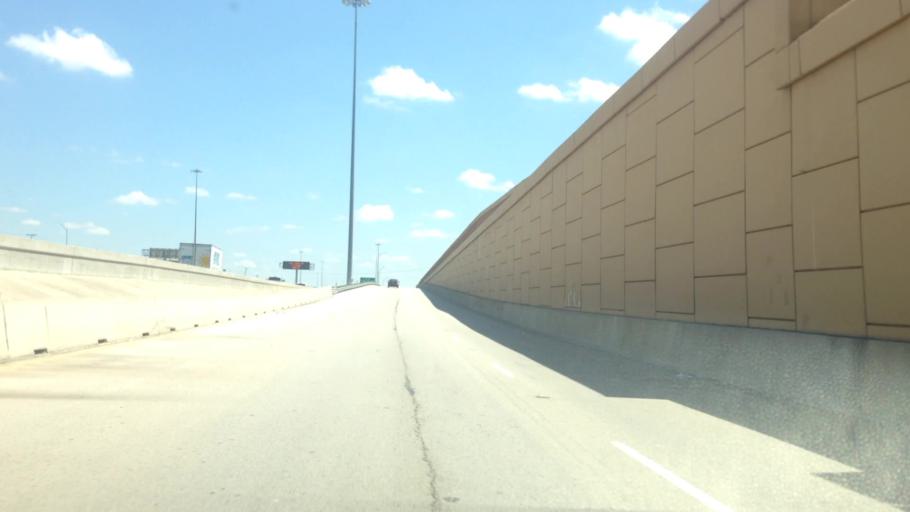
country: US
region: Texas
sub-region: Tarrant County
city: Watauga
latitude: 32.8392
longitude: -97.2765
